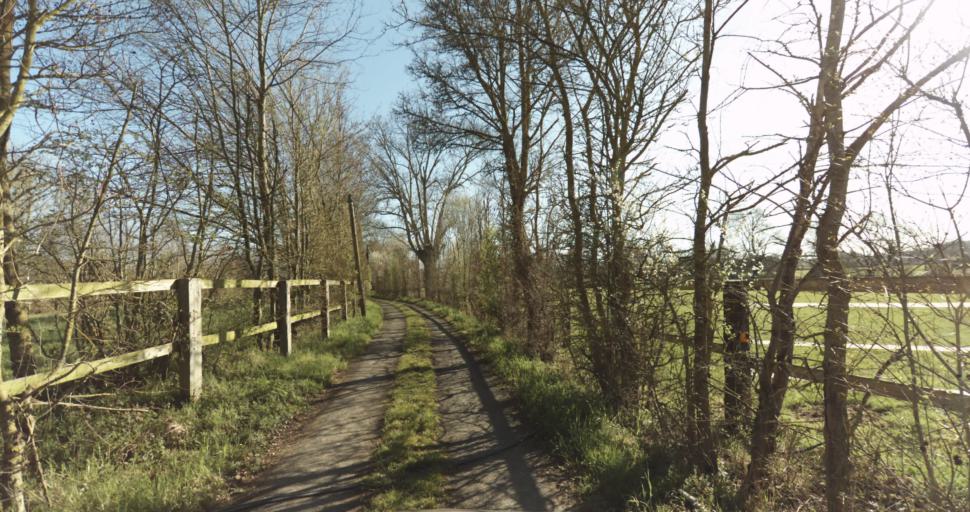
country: FR
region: Lower Normandy
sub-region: Departement du Calvados
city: Saint-Pierre-sur-Dives
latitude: 49.0455
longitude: 0.0594
